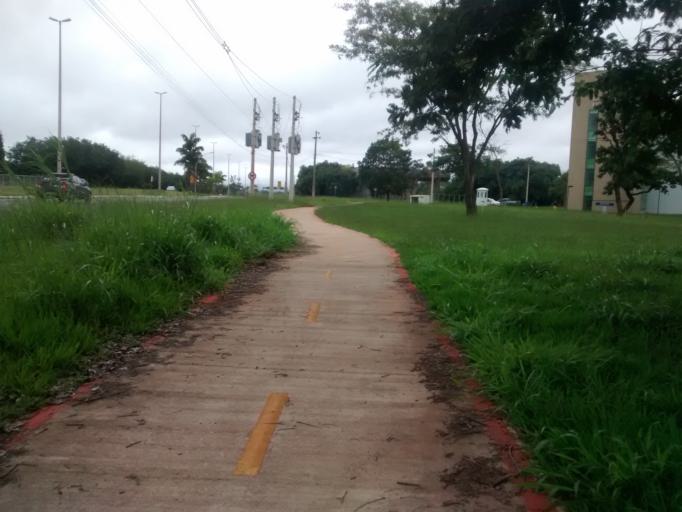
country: BR
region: Federal District
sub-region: Brasilia
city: Brasilia
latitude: -15.7720
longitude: -47.8720
